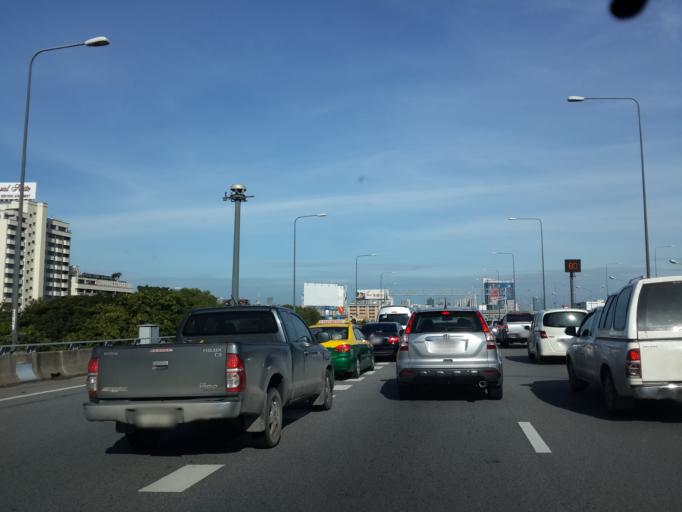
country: TH
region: Bangkok
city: Watthana
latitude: 13.7491
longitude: 100.5999
